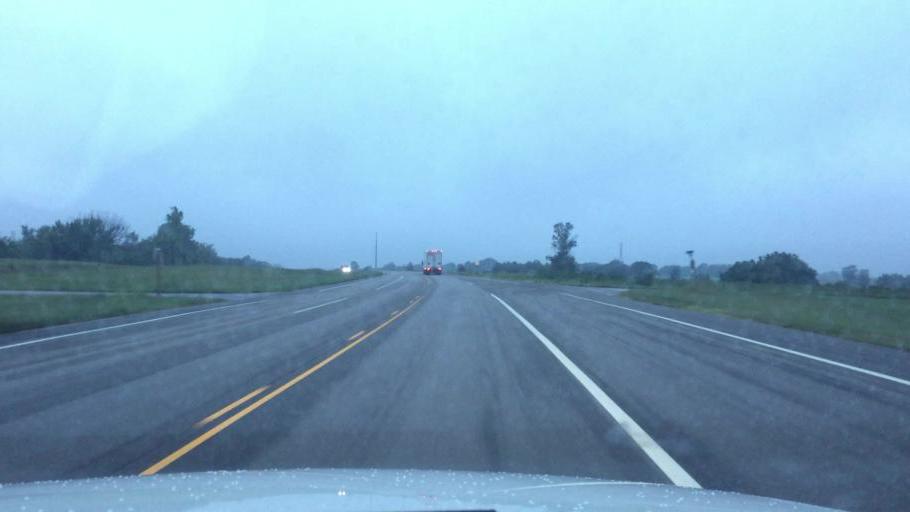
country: US
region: Kansas
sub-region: Montgomery County
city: Cherryvale
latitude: 37.4571
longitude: -95.4819
